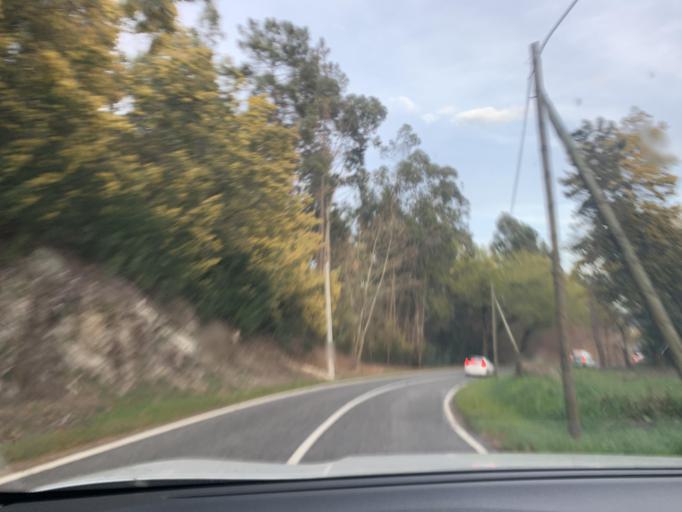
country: PT
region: Viseu
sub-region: Viseu
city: Viseu
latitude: 40.5948
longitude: -7.9984
